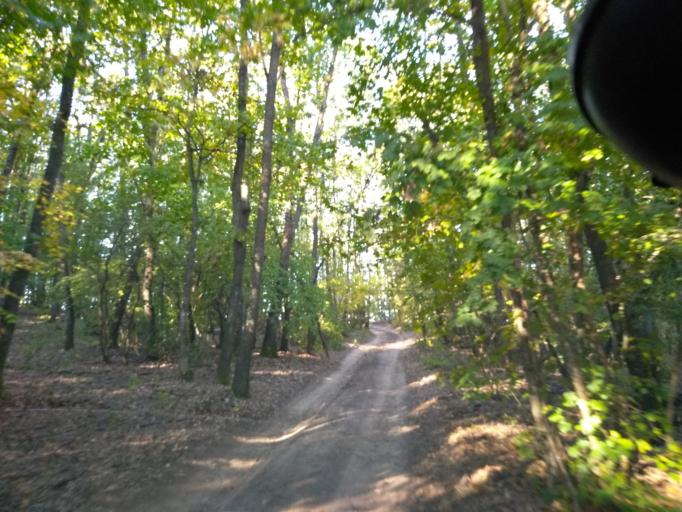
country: RO
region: Timis
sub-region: Comuna Bogda
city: Bogda
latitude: 45.9236
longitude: 21.6146
